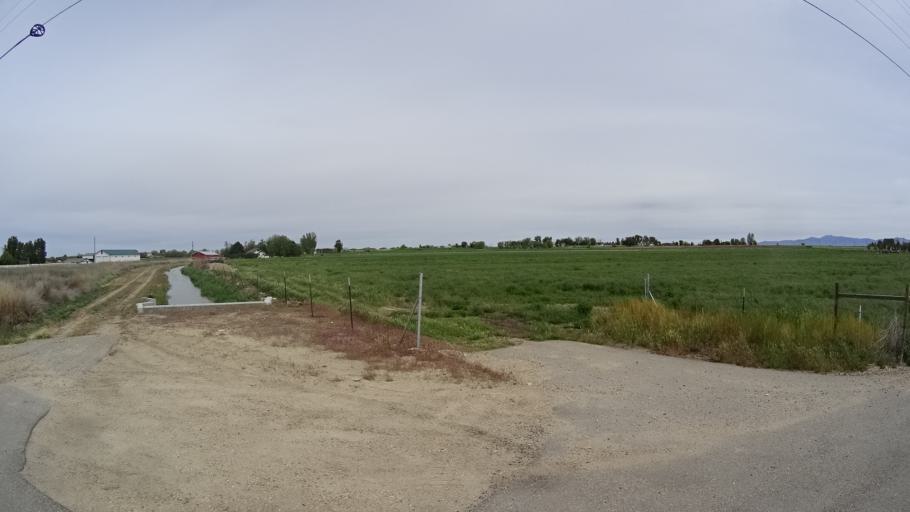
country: US
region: Idaho
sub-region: Ada County
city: Kuna
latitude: 43.5612
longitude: -116.4620
